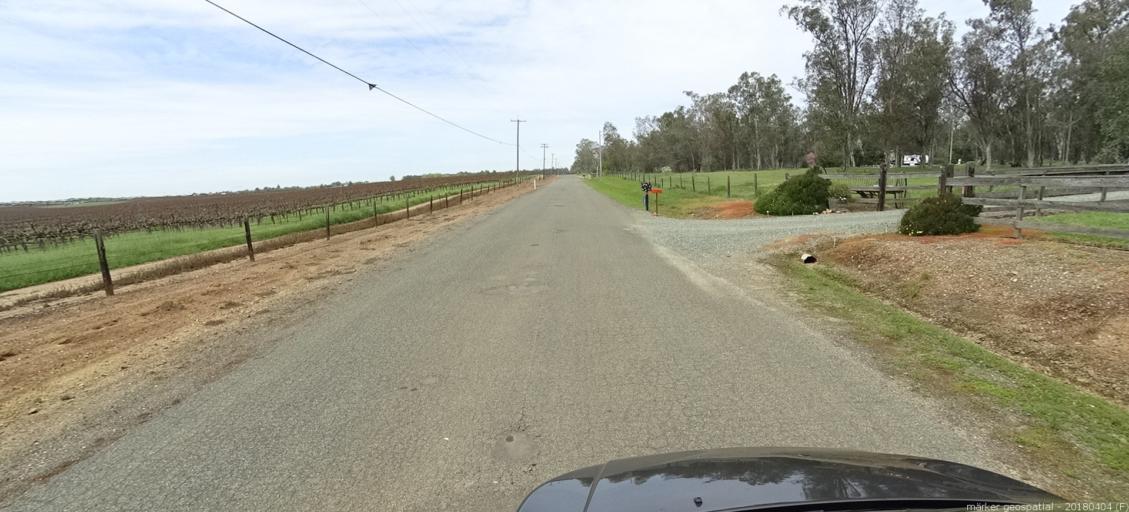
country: US
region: California
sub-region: Sacramento County
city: Clay
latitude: 38.2929
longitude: -121.1613
